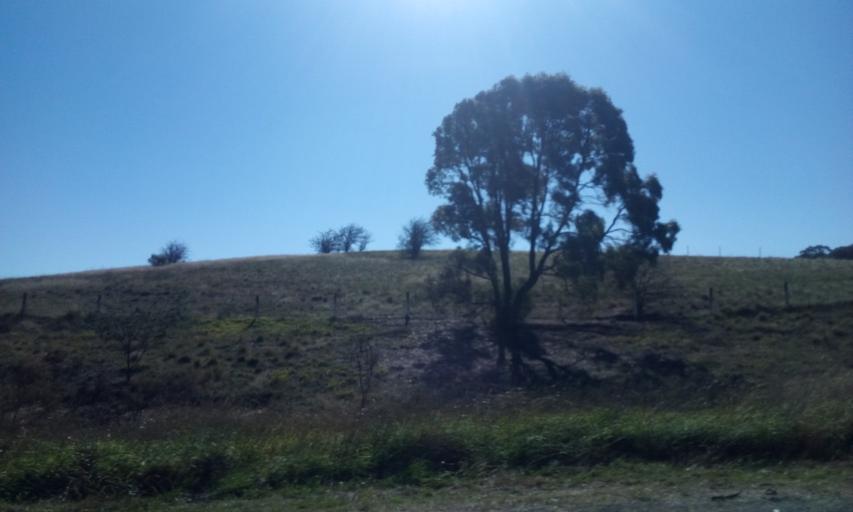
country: AU
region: New South Wales
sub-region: Goulburn Mulwaree
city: Goulburn
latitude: -34.7796
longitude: 149.6727
